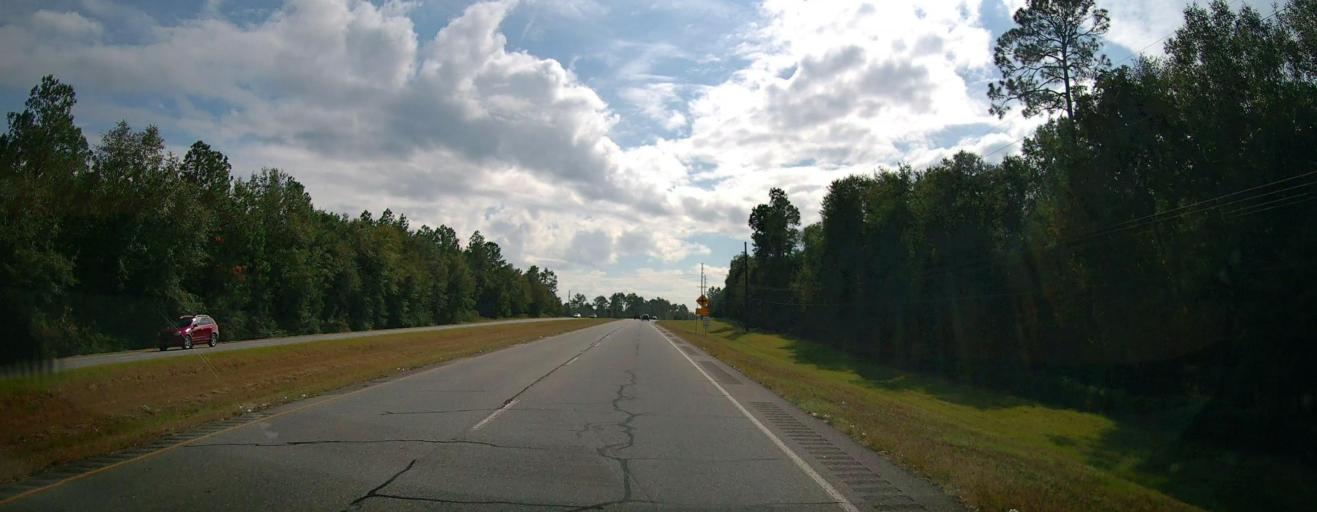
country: US
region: Georgia
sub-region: Mitchell County
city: Camilla
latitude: 31.3199
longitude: -84.1739
